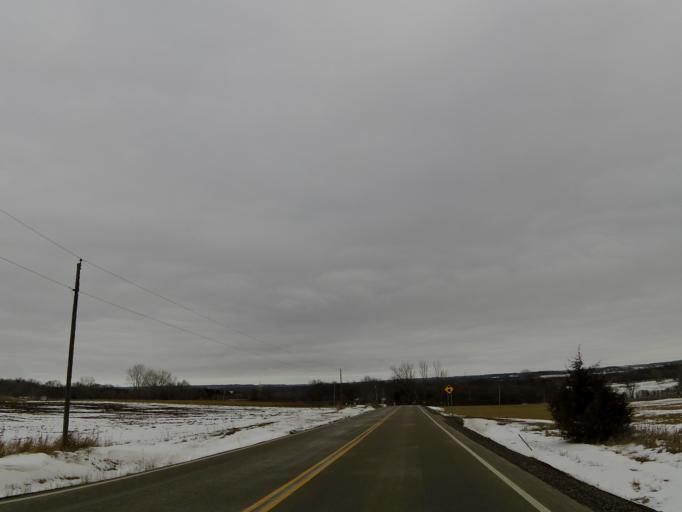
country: US
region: Wisconsin
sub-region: Pierce County
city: Prescott
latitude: 44.8190
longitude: -92.8045
